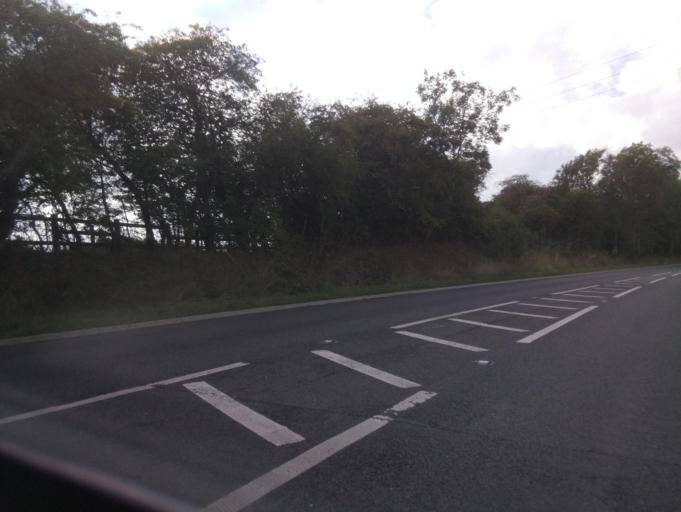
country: GB
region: England
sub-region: Darlington
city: High Coniscliffe
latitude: 54.4671
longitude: -1.6606
